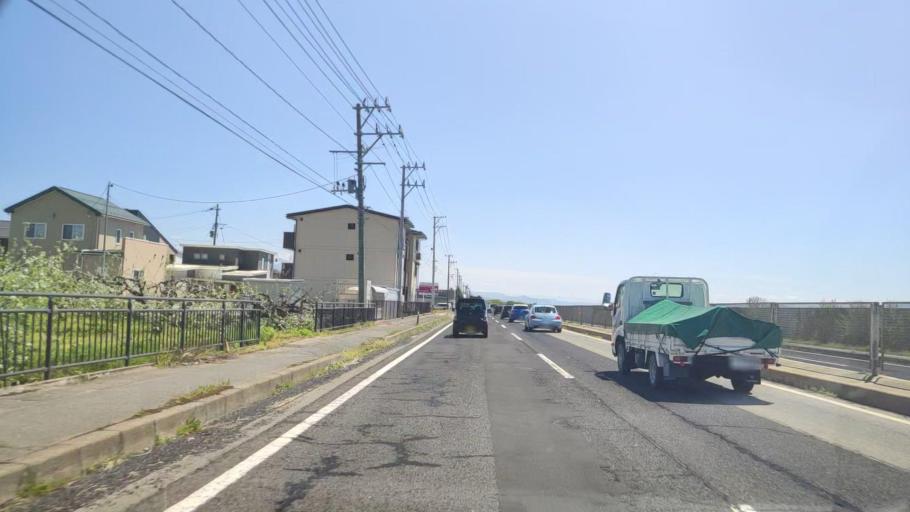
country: JP
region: Yamagata
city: Higashine
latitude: 38.4120
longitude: 140.3745
